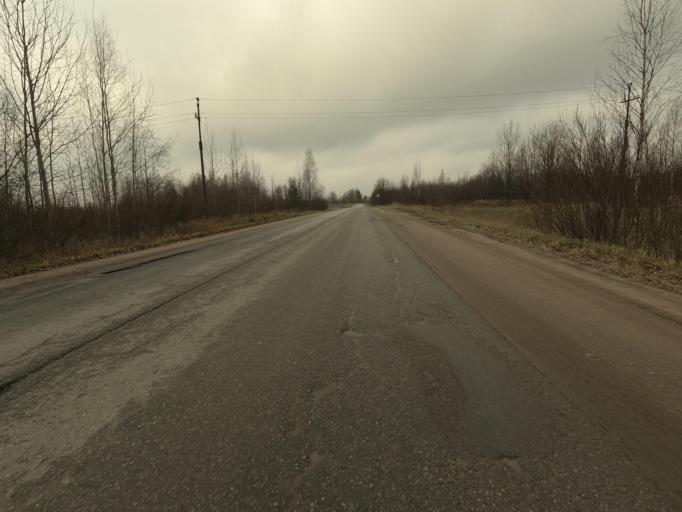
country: RU
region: Leningrad
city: Lyuban'
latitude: 59.4840
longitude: 31.2644
